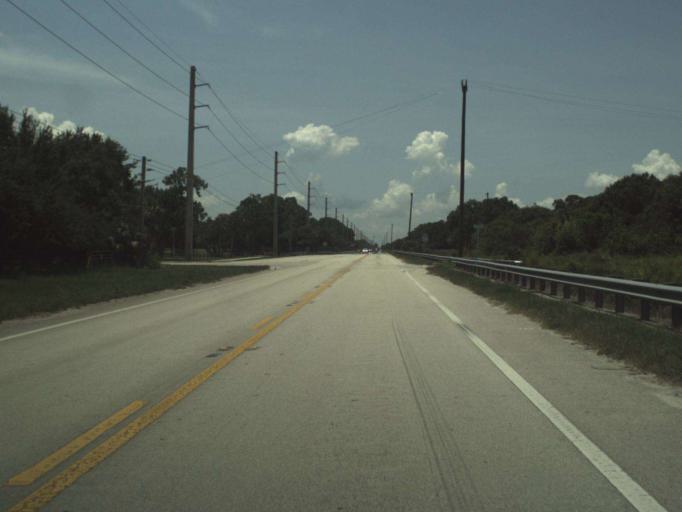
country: US
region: Florida
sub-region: Saint Lucie County
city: Lakewood Park
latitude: 27.5437
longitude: -80.4147
